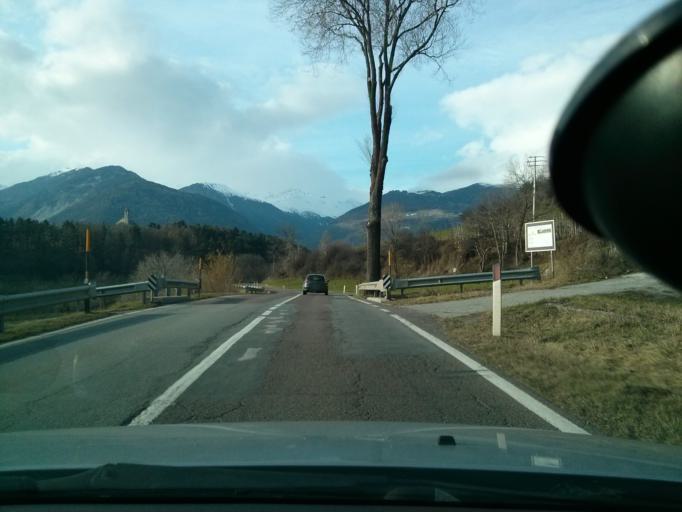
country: IT
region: Trentino-Alto Adige
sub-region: Bolzano
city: Glorenza
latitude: 46.6789
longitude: 10.5696
